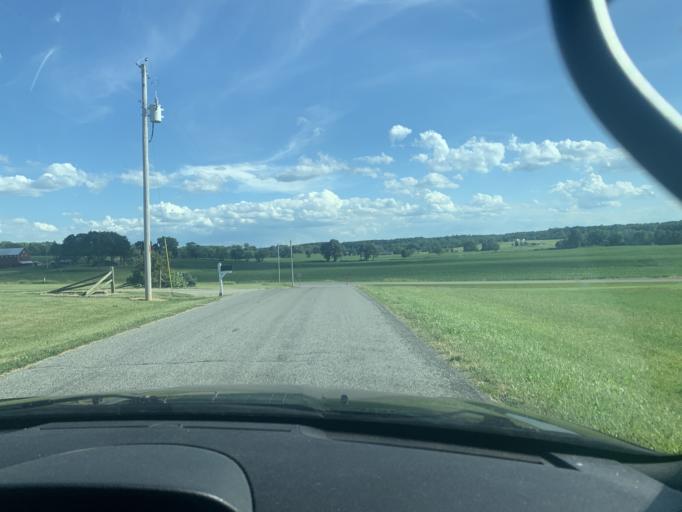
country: US
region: Ohio
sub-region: Logan County
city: De Graff
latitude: 40.2811
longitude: -83.8776
